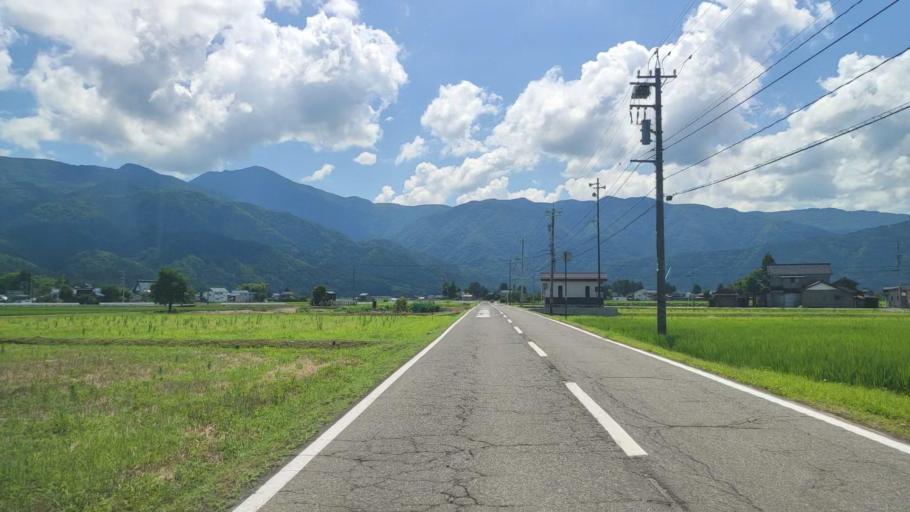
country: JP
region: Fukui
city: Ono
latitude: 35.9603
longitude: 136.5327
